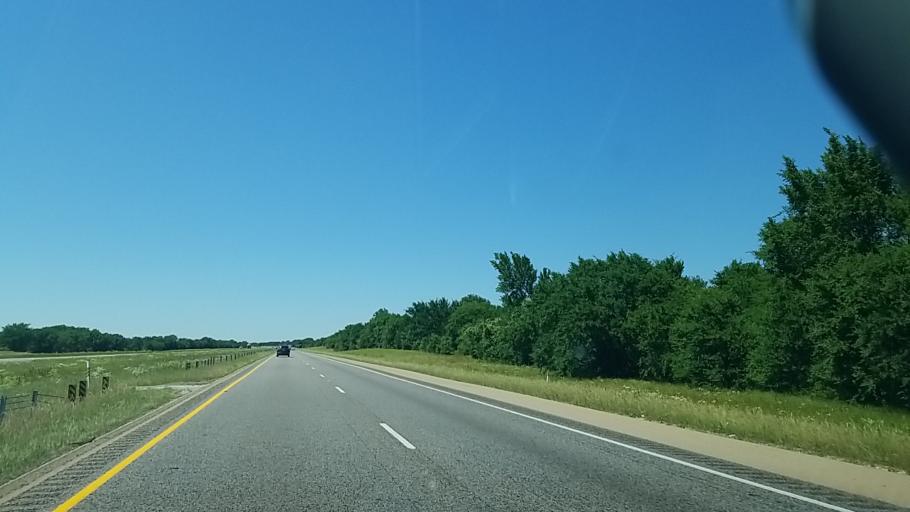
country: US
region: Texas
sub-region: Freestone County
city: Fairfield
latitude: 31.6735
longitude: -96.1636
